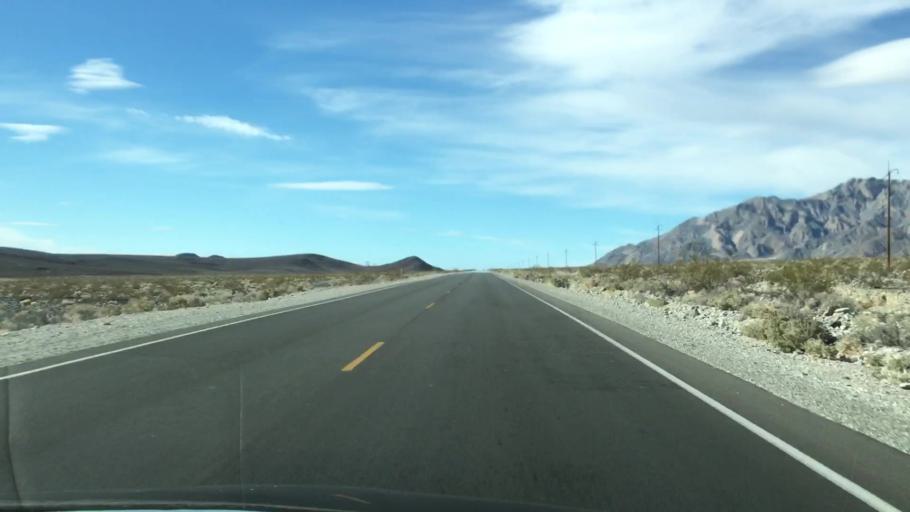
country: US
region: Nevada
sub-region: Nye County
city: Pahrump
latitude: 36.3286
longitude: -116.5712
